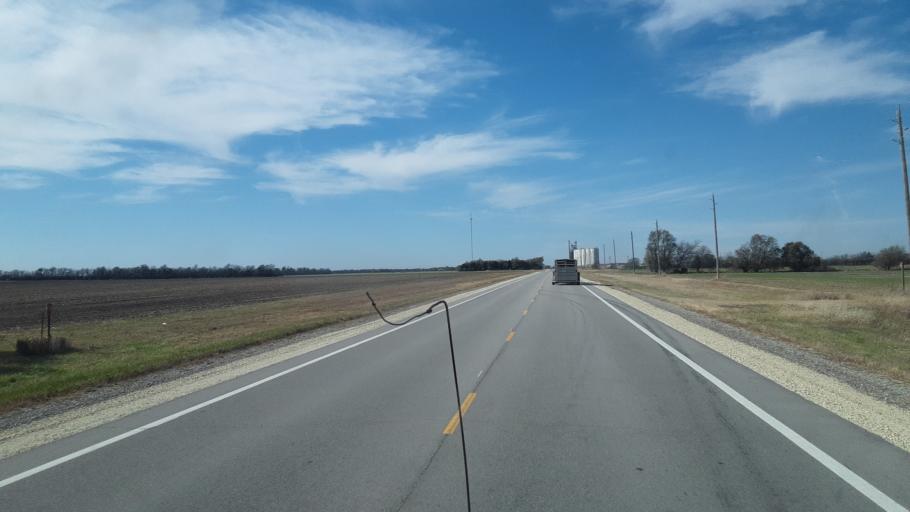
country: US
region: Kansas
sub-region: McPherson County
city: Moundridge
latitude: 38.3769
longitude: -97.4479
